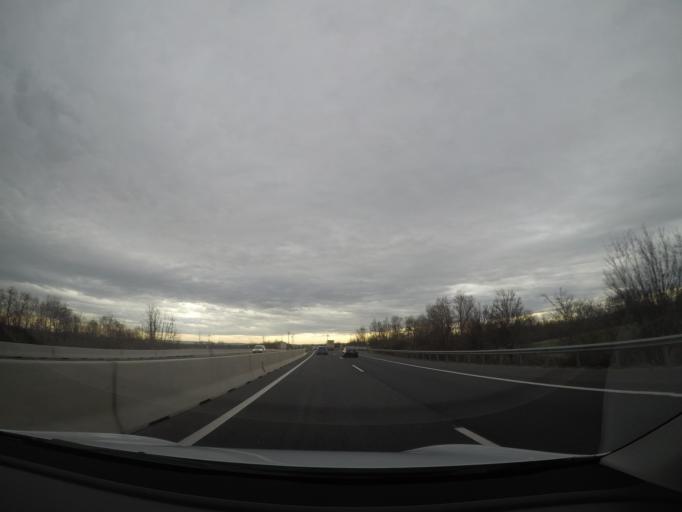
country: AT
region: Lower Austria
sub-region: Politischer Bezirk Modling
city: Munchendorf
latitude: 48.0138
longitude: 16.3656
